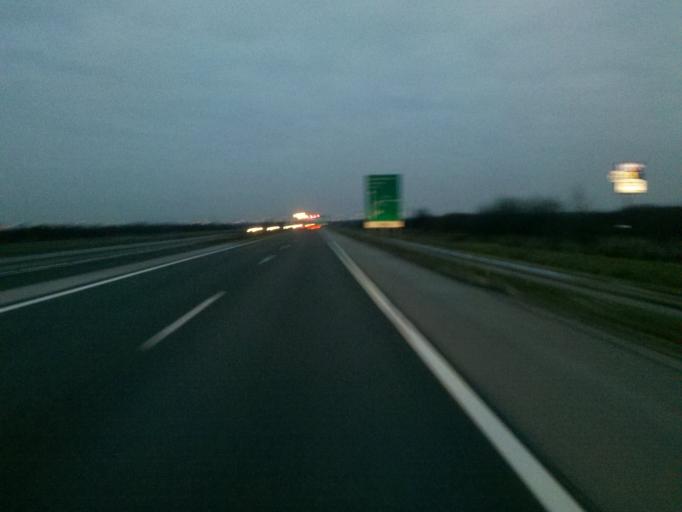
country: HR
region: Grad Zagreb
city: Odra
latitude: 45.7482
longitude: 16.0265
